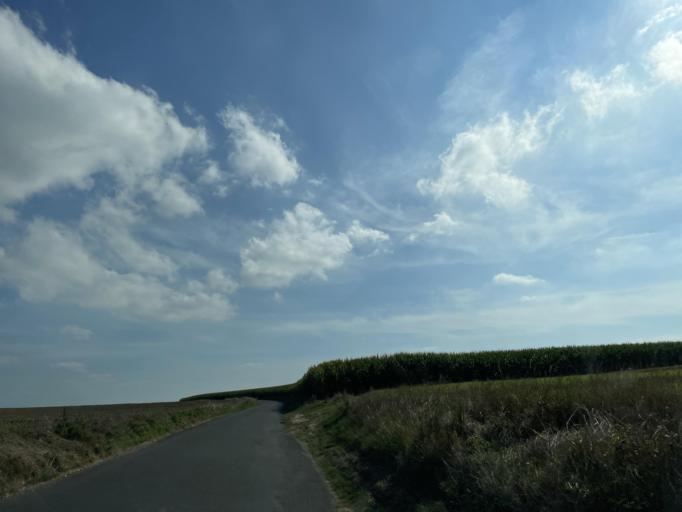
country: FR
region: Haute-Normandie
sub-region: Departement de la Seine-Maritime
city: Criel-sur-Mer
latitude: 50.0363
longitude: 1.3423
